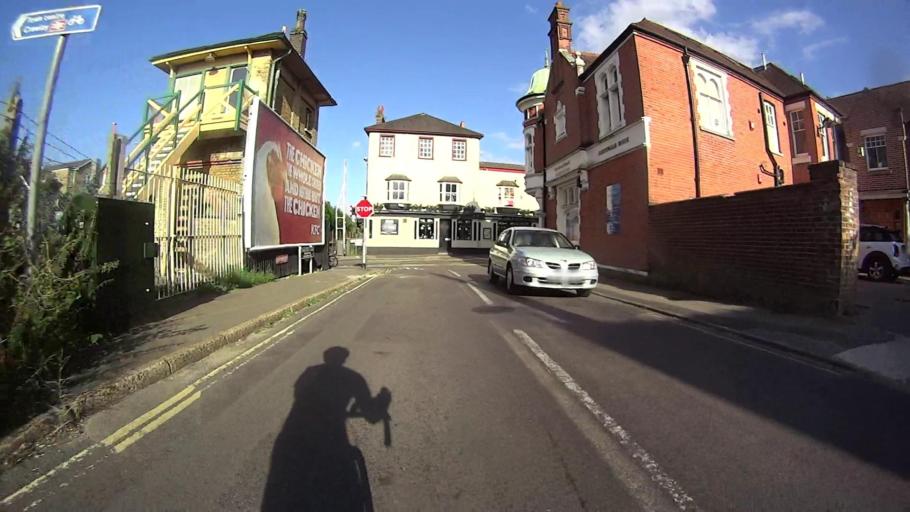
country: GB
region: England
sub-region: West Sussex
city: Crawley
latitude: 51.1125
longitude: -0.1912
